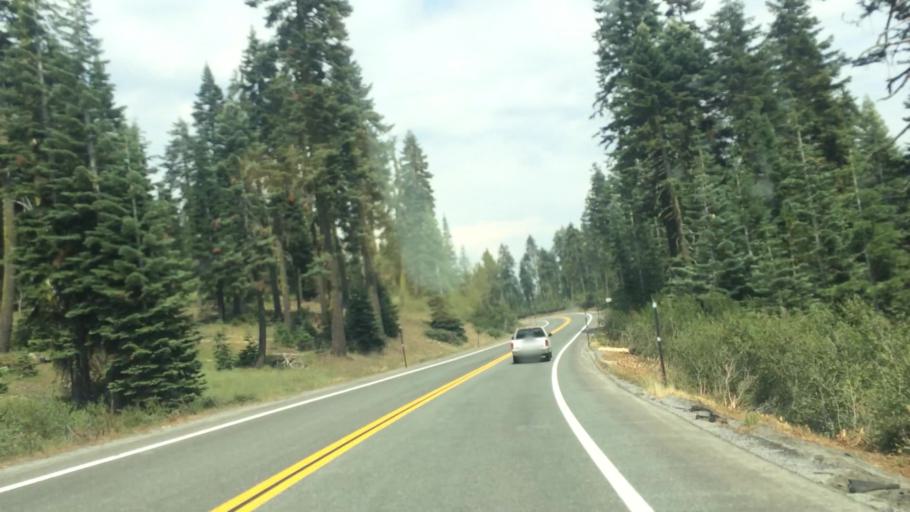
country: US
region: California
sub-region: Calaveras County
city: Arnold
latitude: 38.5862
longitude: -120.2360
